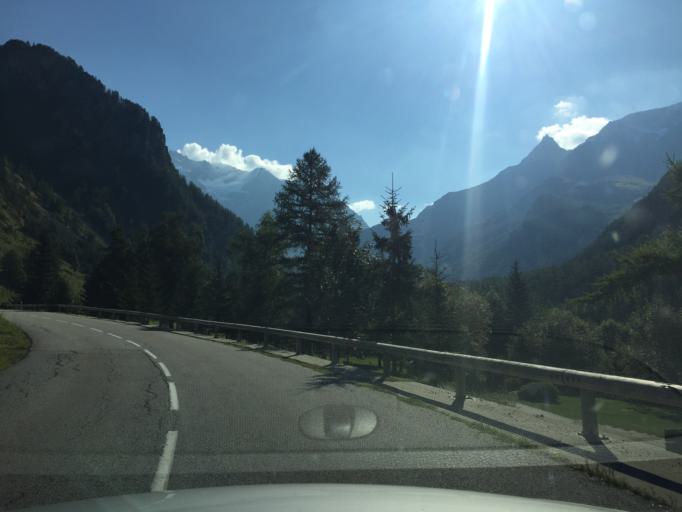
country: FR
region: Rhone-Alpes
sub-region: Departement de la Savoie
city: Belle-Plagne
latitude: 45.5313
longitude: 6.7756
